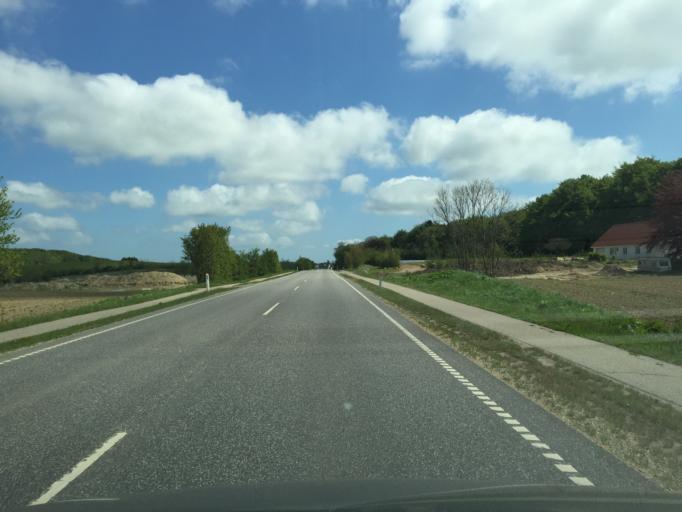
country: DK
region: Zealand
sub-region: Vordingborg Kommune
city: Nyrad
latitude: 54.9964
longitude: 12.0443
